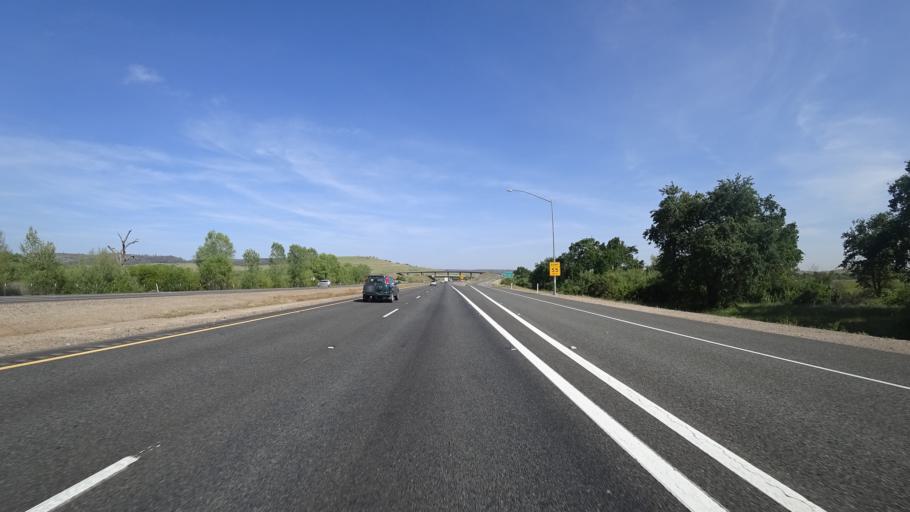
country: US
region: California
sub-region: Butte County
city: Thermalito
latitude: 39.5859
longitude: -121.6295
